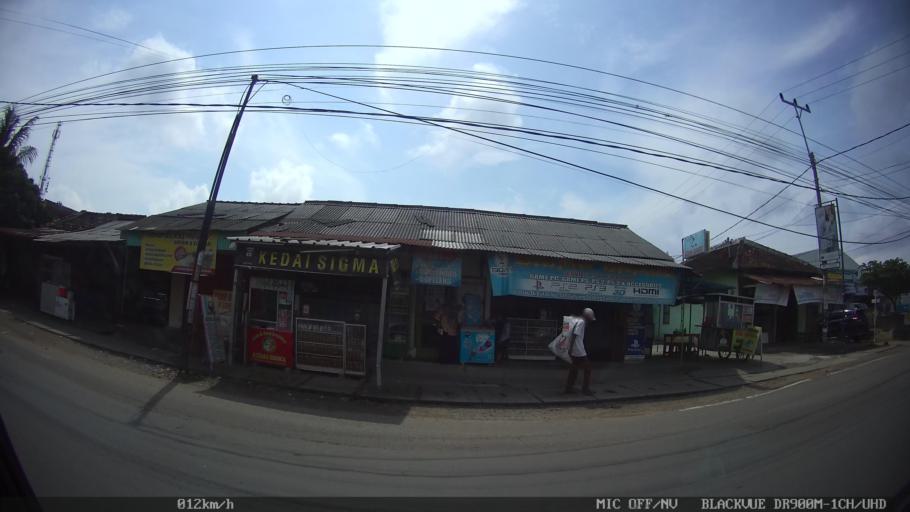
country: ID
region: Lampung
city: Kedaton
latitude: -5.3690
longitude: 105.2749
